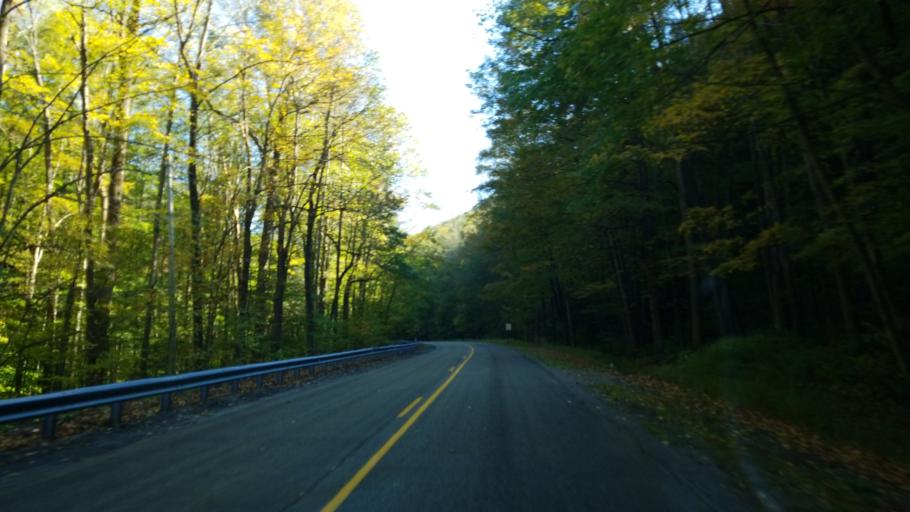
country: US
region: Pennsylvania
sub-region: Clearfield County
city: Shiloh
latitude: 41.2557
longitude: -78.3859
